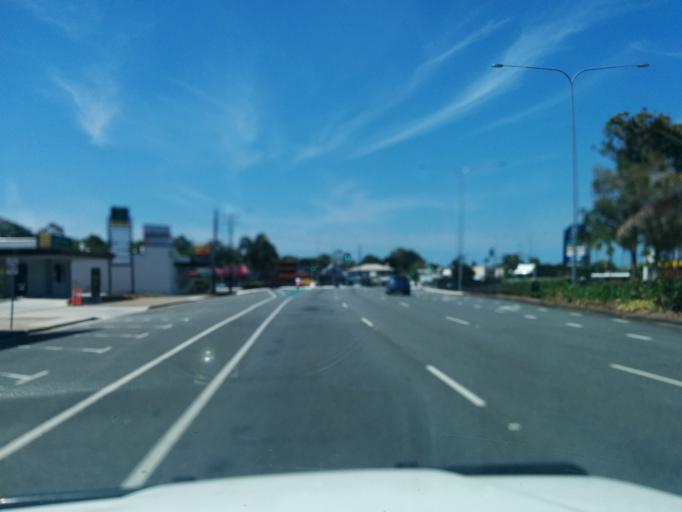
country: AU
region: Queensland
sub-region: Cairns
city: Woree
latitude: -16.9438
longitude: 145.7384
